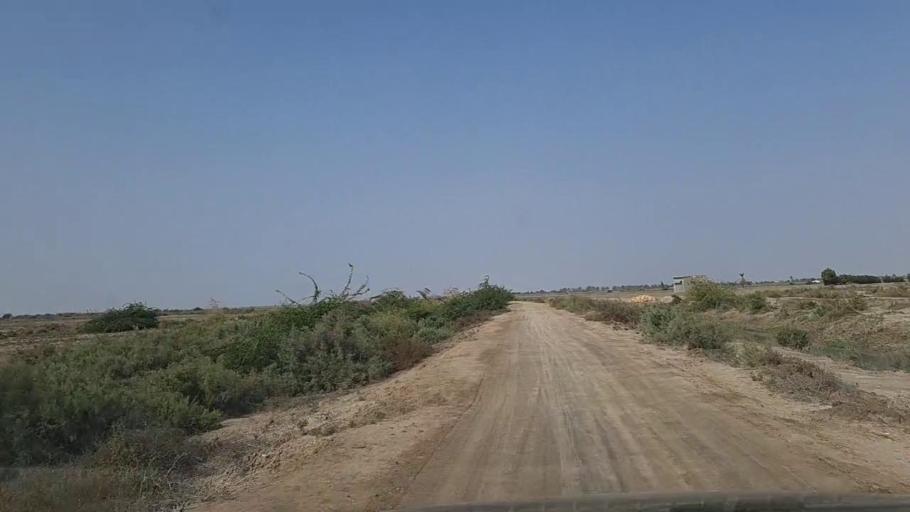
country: PK
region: Sindh
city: Gharo
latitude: 24.7039
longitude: 67.5826
